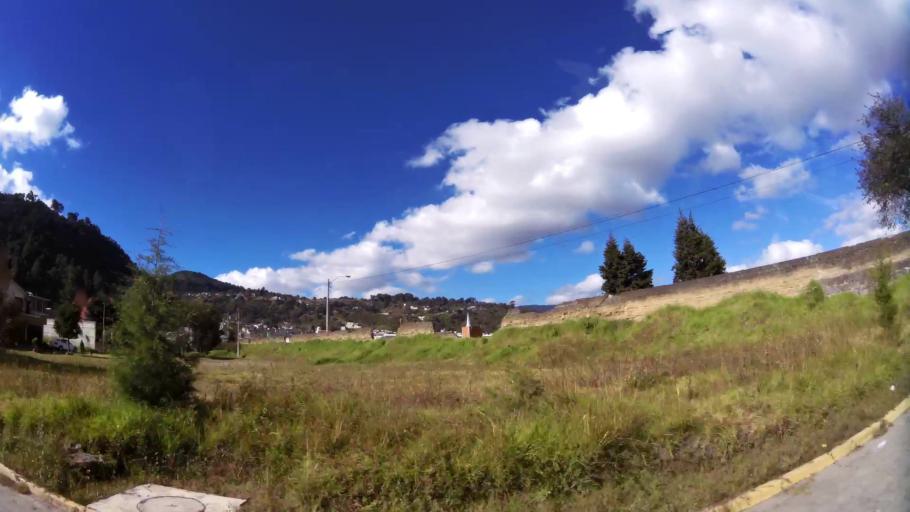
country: GT
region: Quetzaltenango
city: Quetzaltenango
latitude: 14.8303
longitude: -91.5105
